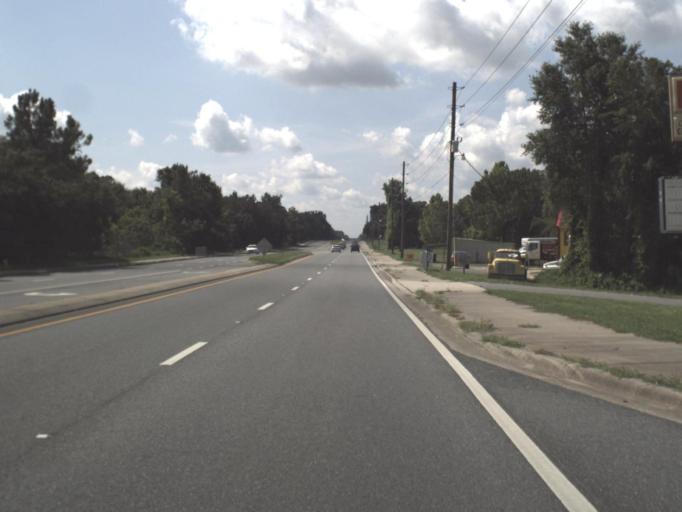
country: US
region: Florida
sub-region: Citrus County
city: Inverness Highlands South
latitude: 28.8072
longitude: -82.3130
